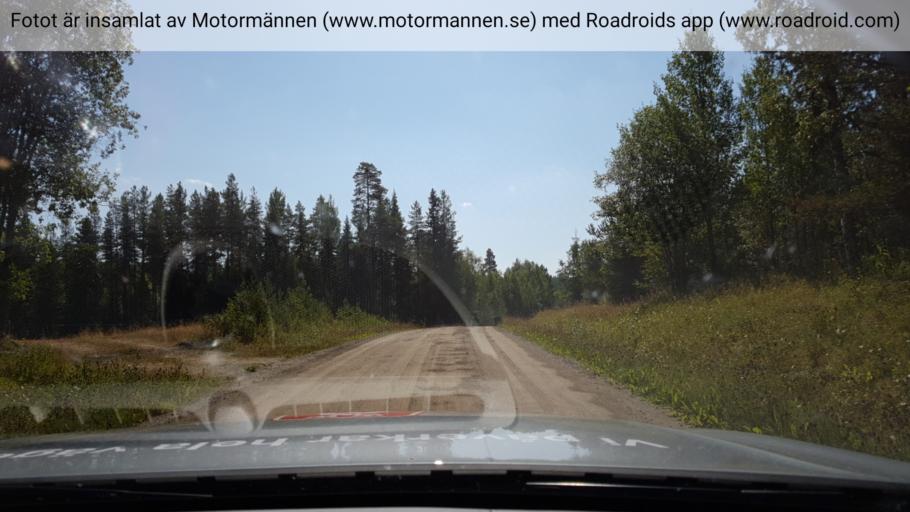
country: SE
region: Jaemtland
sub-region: Stroemsunds Kommun
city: Stroemsund
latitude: 63.3332
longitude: 15.4628
